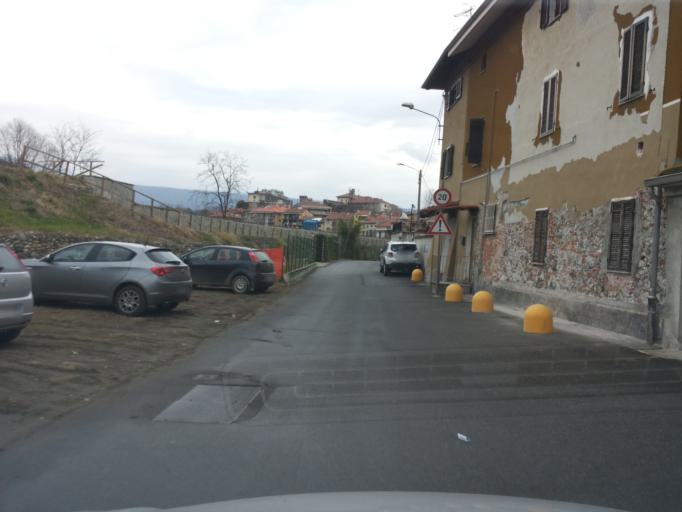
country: IT
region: Piedmont
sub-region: Provincia di Torino
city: Ivrea
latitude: 45.4632
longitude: 7.8681
